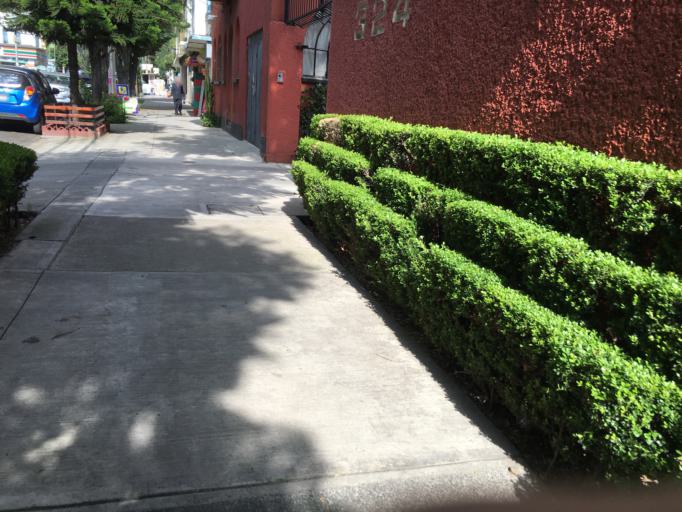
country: MX
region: Mexico City
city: Colonia del Valle
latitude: 19.3761
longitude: -99.1689
